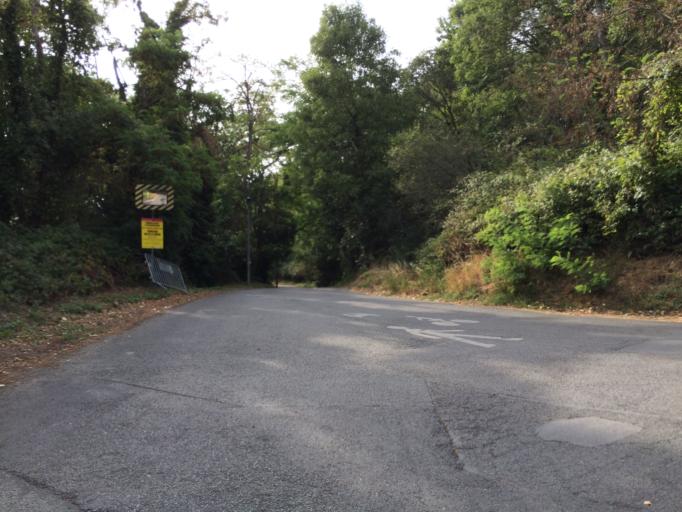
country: FR
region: Ile-de-France
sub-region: Departement de l'Essonne
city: Orsay
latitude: 48.7089
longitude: 2.2012
